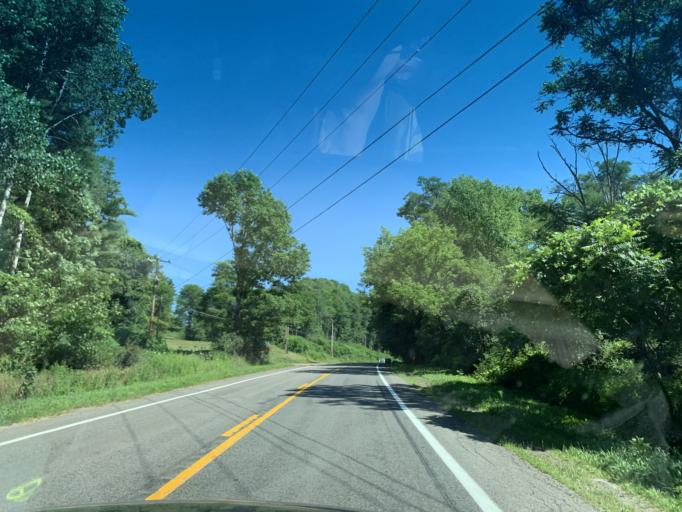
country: US
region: New York
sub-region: Delaware County
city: Sidney
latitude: 42.3239
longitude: -75.4113
